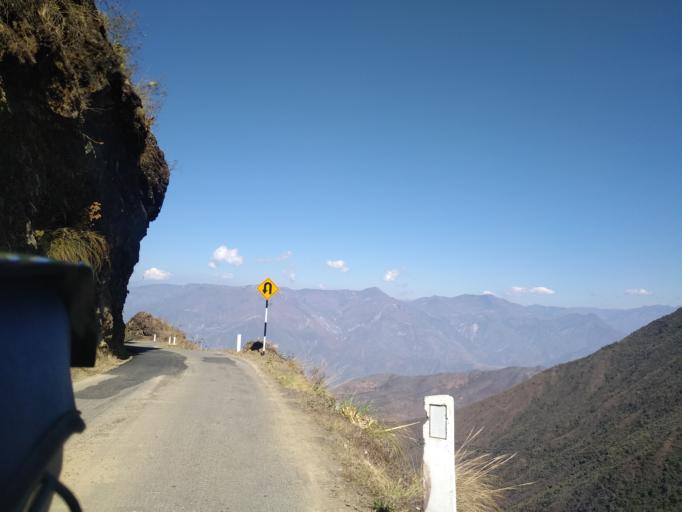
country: PE
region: Amazonas
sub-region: Provincia de Chachapoyas
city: Balsas
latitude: -6.7943
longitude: -77.9427
